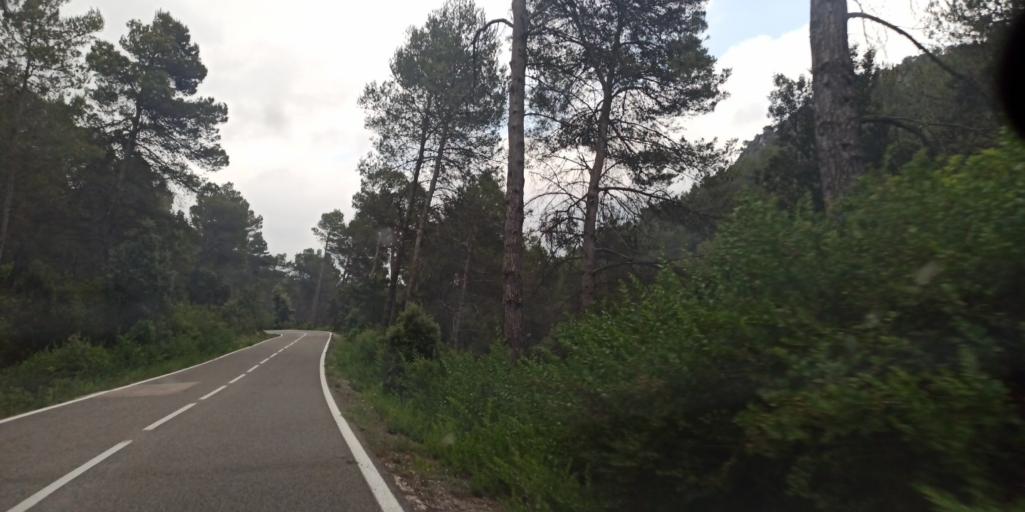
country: ES
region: Catalonia
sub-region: Provincia de Tarragona
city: Querol
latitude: 41.3809
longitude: 1.4728
